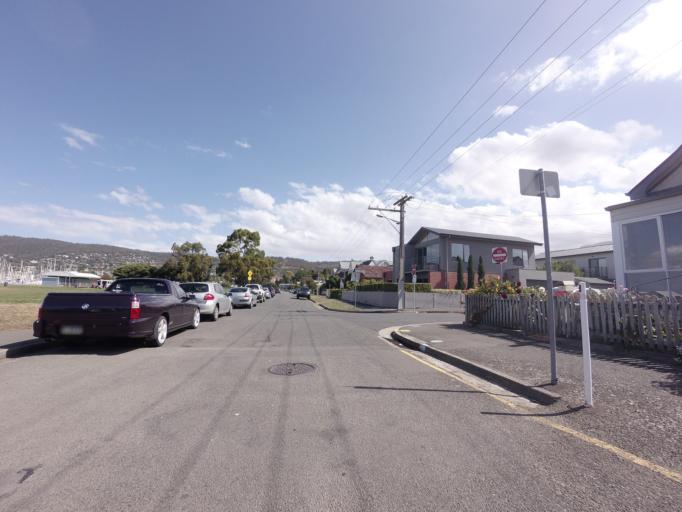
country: AU
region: Tasmania
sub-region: Hobart
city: Sandy Bay
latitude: -42.8950
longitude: 147.3331
